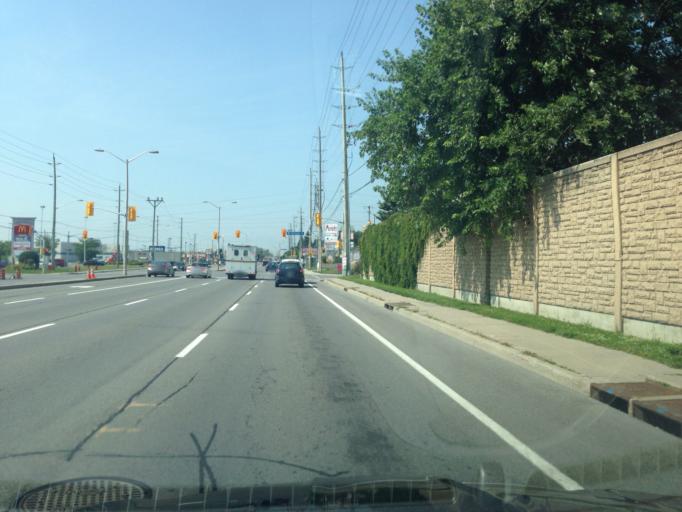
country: CA
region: Ontario
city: Ottawa
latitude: 45.4187
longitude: -75.5976
